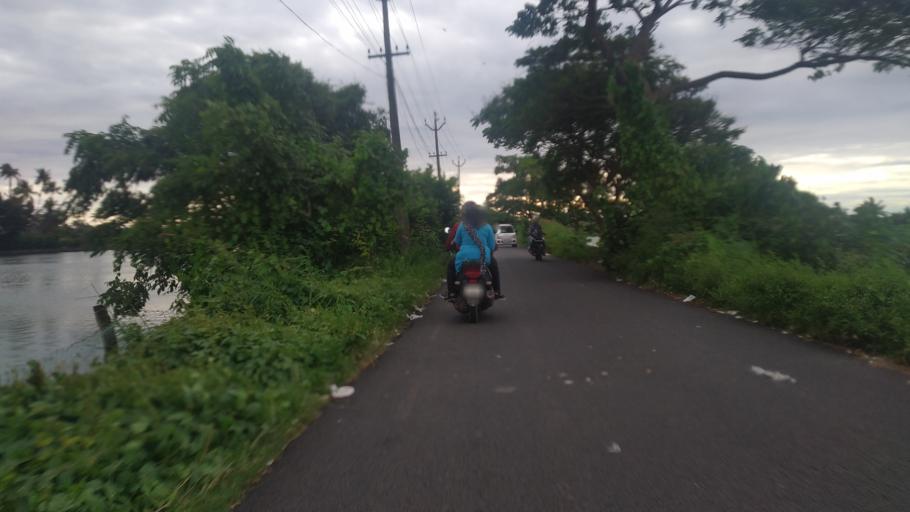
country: IN
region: Kerala
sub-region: Alappuzha
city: Arukutti
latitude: 9.8595
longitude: 76.2836
